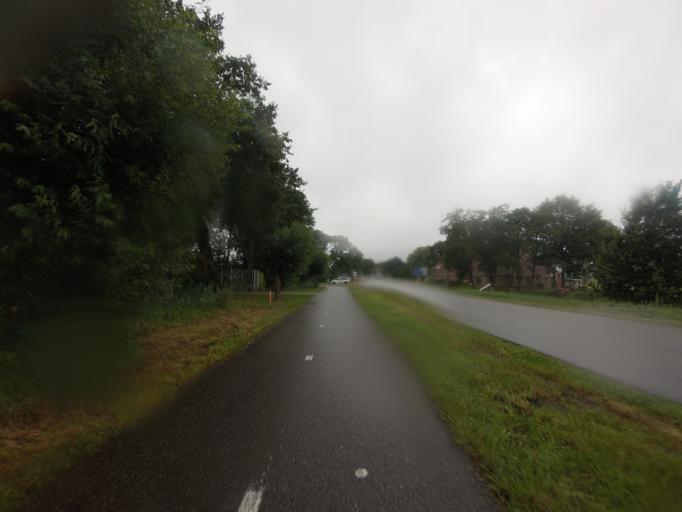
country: NL
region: Friesland
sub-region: Gemeente Tytsjerksteradiel
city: Garyp
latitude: 53.1334
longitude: 5.9438
